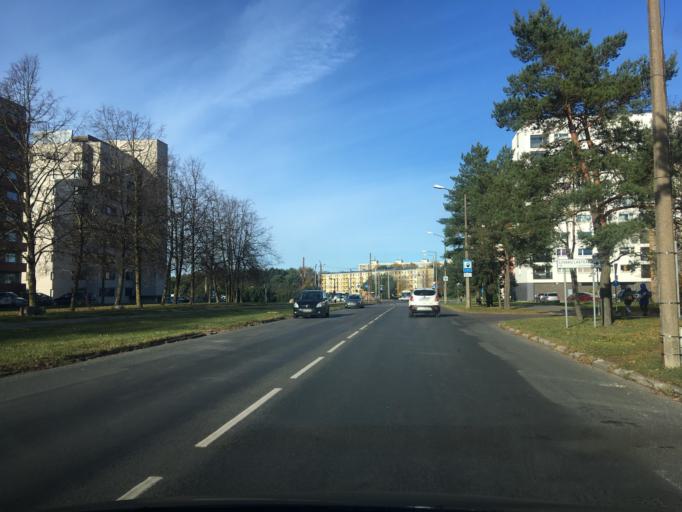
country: EE
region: Harju
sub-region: Tallinna linn
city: Tallinn
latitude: 59.3973
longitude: 24.6828
